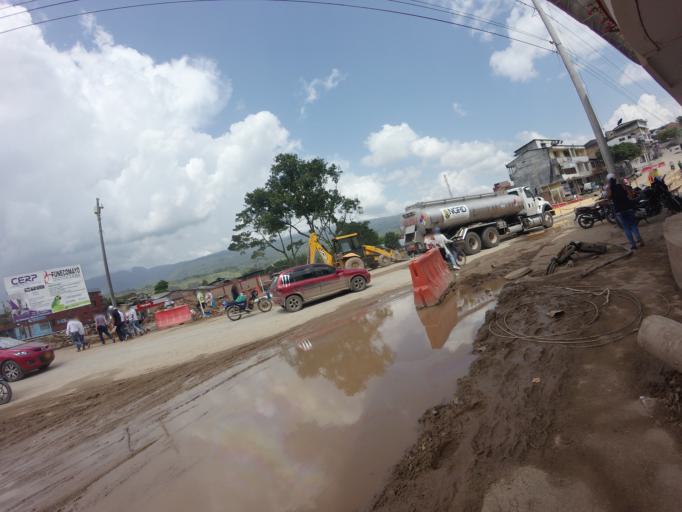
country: CO
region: Putumayo
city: Mocoa
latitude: 1.1492
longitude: -76.6484
